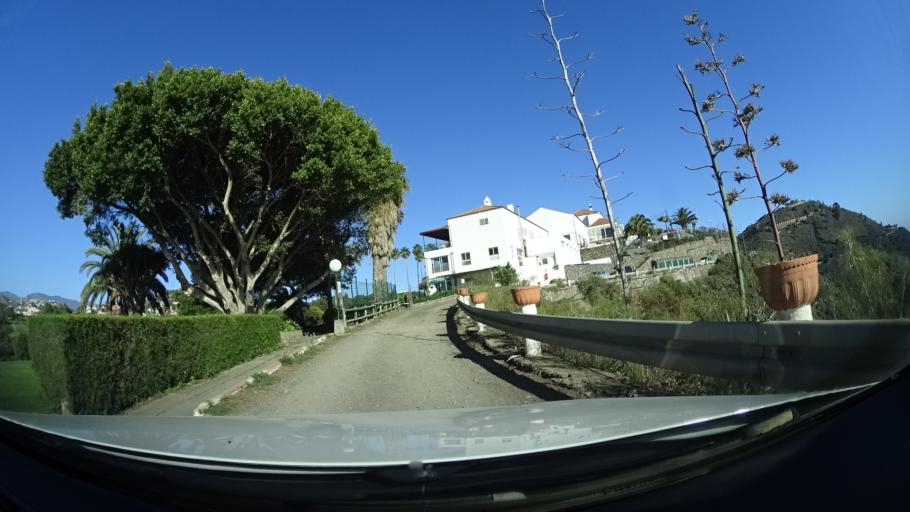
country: ES
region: Canary Islands
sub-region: Provincia de Las Palmas
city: Santa Brigida
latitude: 28.0305
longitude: -15.4597
